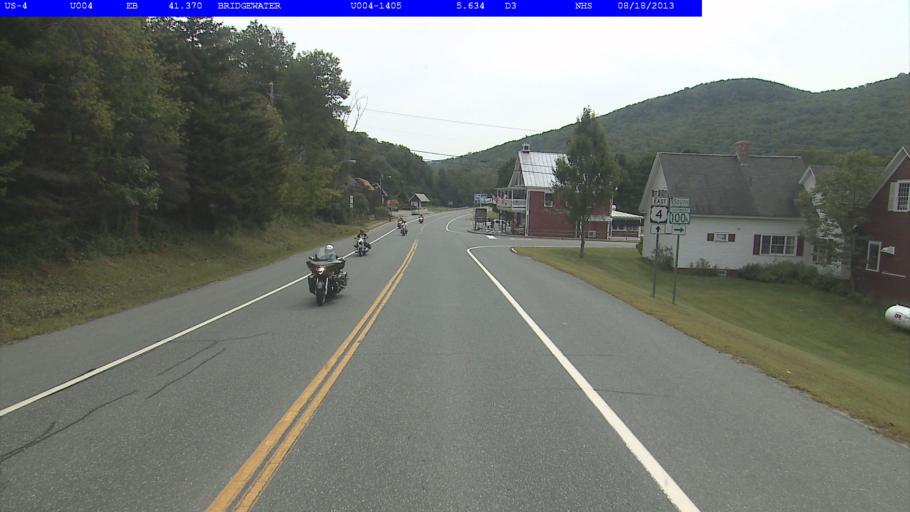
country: US
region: Vermont
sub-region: Windsor County
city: Woodstock
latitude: 43.5883
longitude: -72.6570
